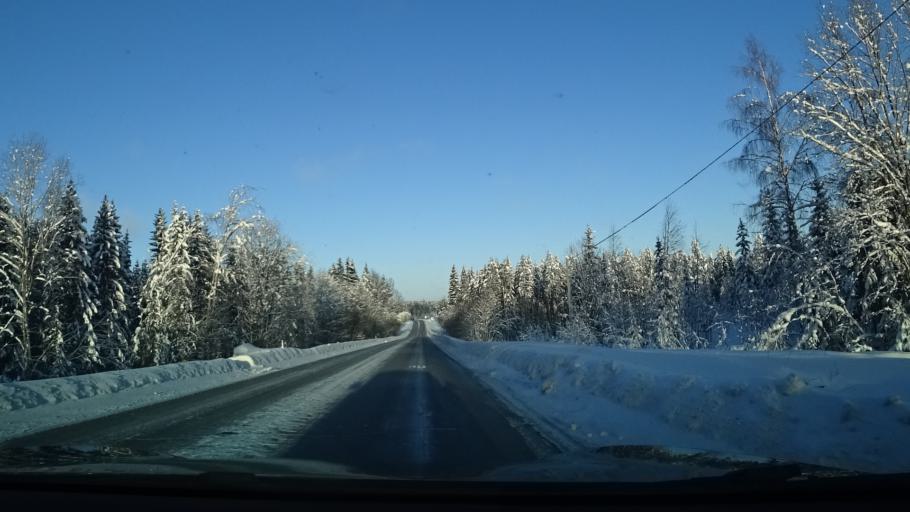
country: FI
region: Northern Savo
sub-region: Varkaus
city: Kangaslampi
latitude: 62.3935
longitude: 28.1475
